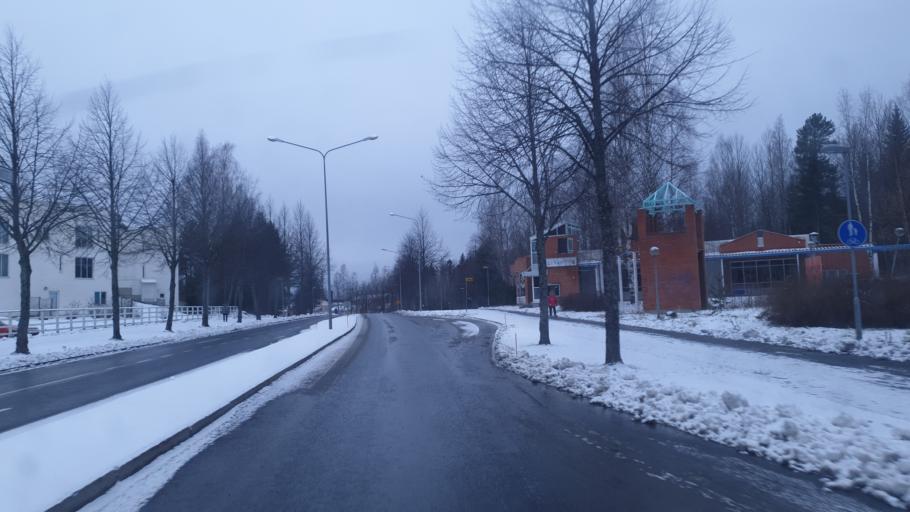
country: FI
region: Northern Savo
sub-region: Kuopio
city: Kuopio
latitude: 62.8356
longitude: 27.6245
